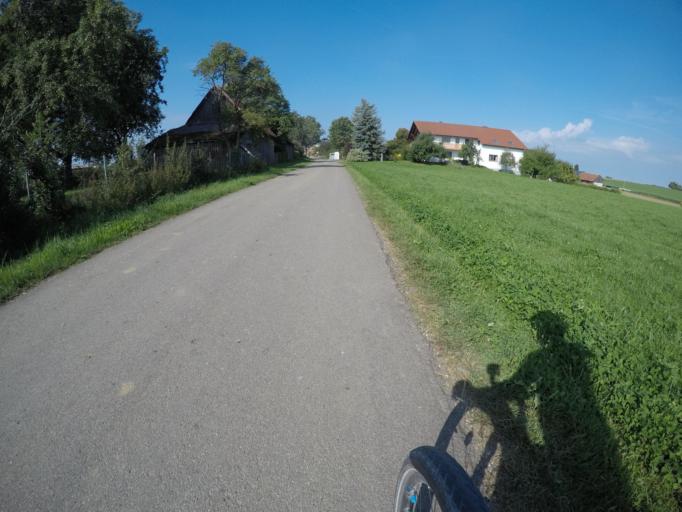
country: DE
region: Baden-Wuerttemberg
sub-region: Regierungsbezirk Stuttgart
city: Bohmenkirch
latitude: 48.6349
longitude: 9.9154
